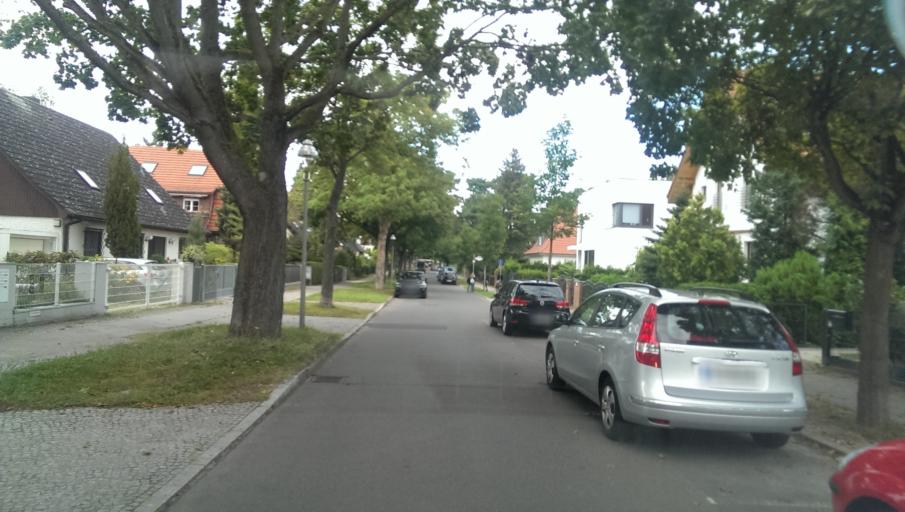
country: DE
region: Brandenburg
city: Teltow
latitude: 52.4134
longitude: 13.2629
